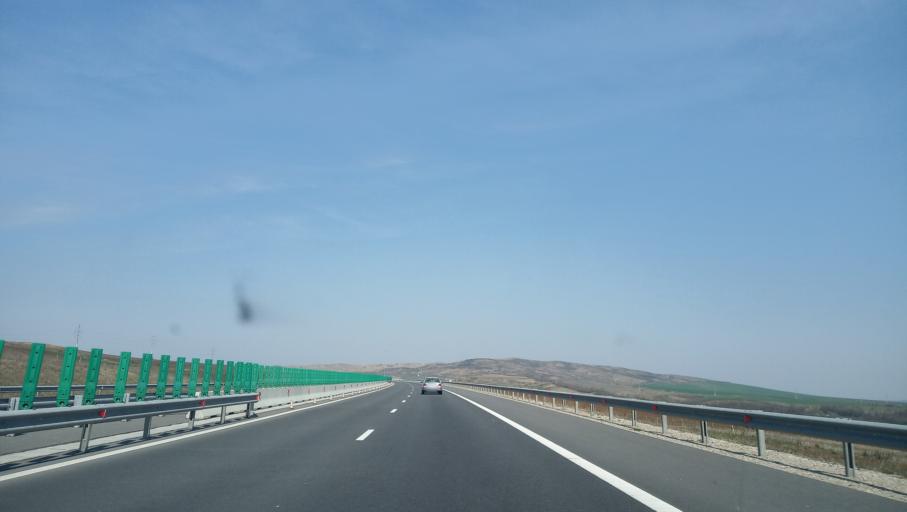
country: RO
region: Alba
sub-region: Comuna Unirea
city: Unirea
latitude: 46.4021
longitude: 23.7964
